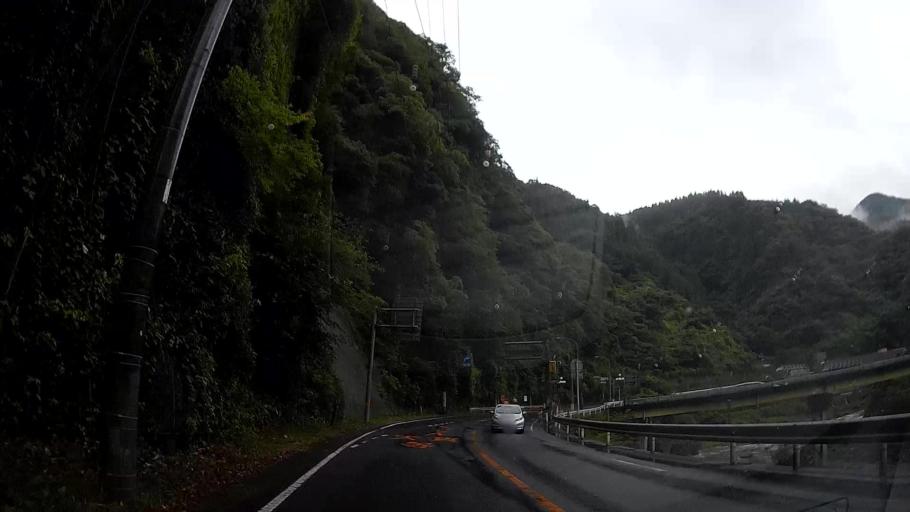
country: JP
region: Oita
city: Tsukawaki
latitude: 33.1863
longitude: 131.0276
